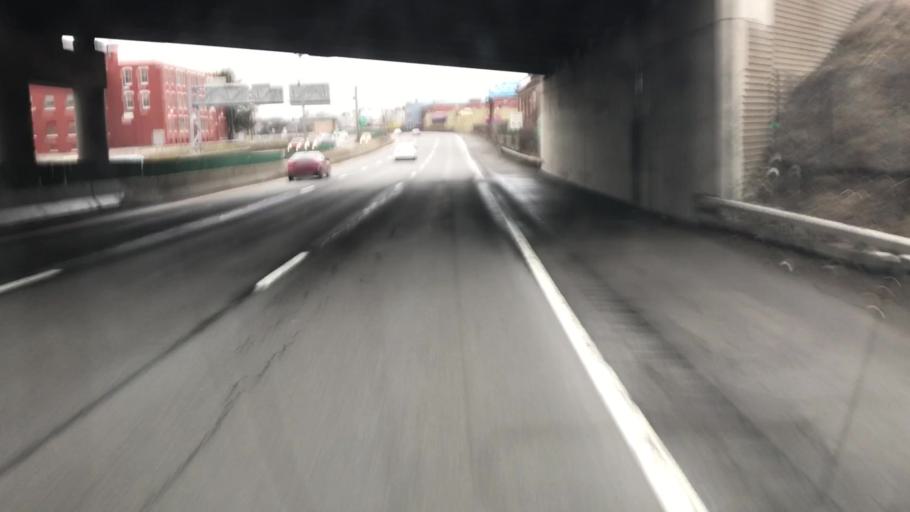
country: US
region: New York
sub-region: Onondaga County
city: Syracuse
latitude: 43.0565
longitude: -76.1534
